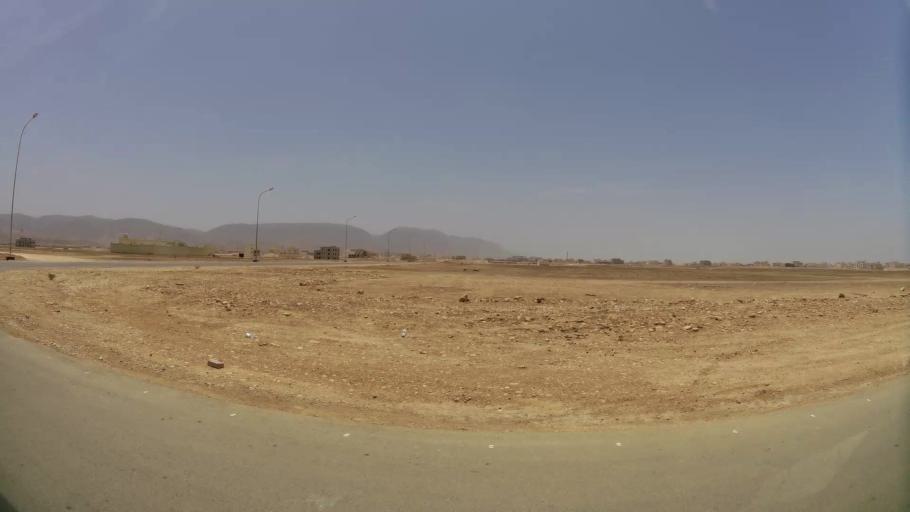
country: OM
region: Zufar
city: Salalah
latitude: 17.0976
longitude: 54.1996
